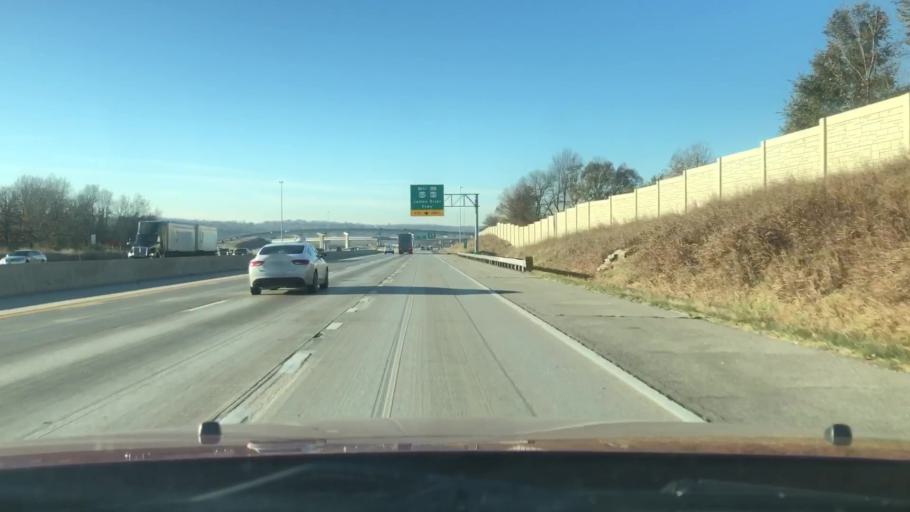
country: US
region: Missouri
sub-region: Greene County
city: Springfield
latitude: 37.1345
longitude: -93.2266
